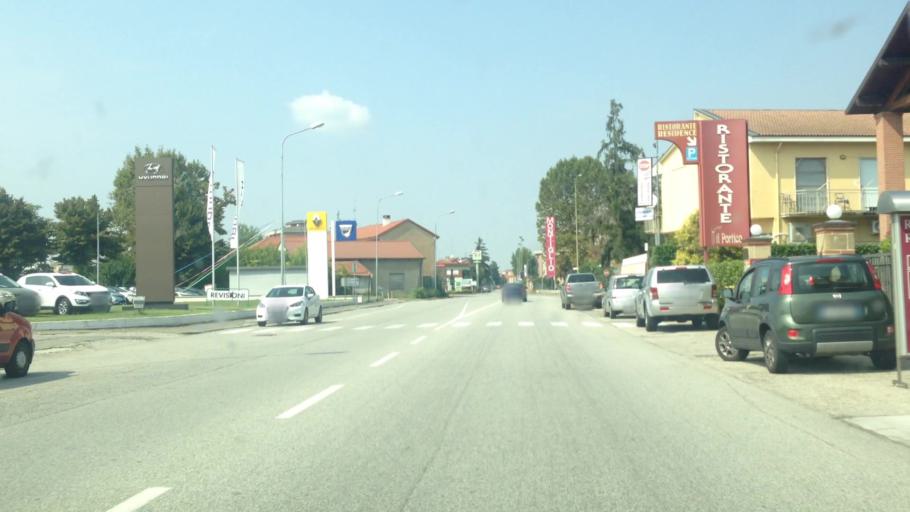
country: IT
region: Piedmont
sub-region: Provincia di Alessandria
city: Casale Monferrato
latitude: 45.1302
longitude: 8.4741
